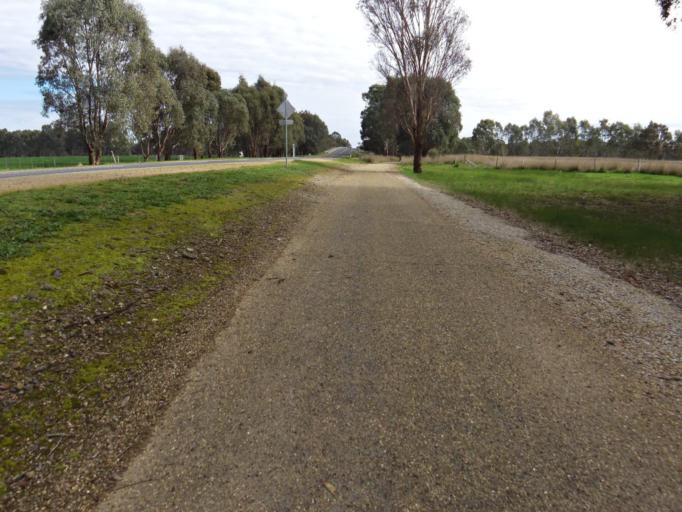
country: AU
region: Victoria
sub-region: Wangaratta
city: Wangaratta
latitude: -36.3961
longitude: 146.3435
